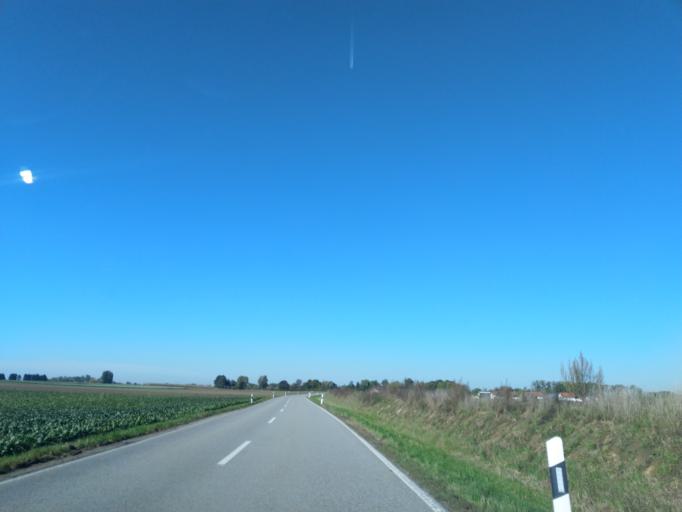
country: DE
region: Bavaria
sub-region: Lower Bavaria
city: Offenberg
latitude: 48.8220
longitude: 12.8726
